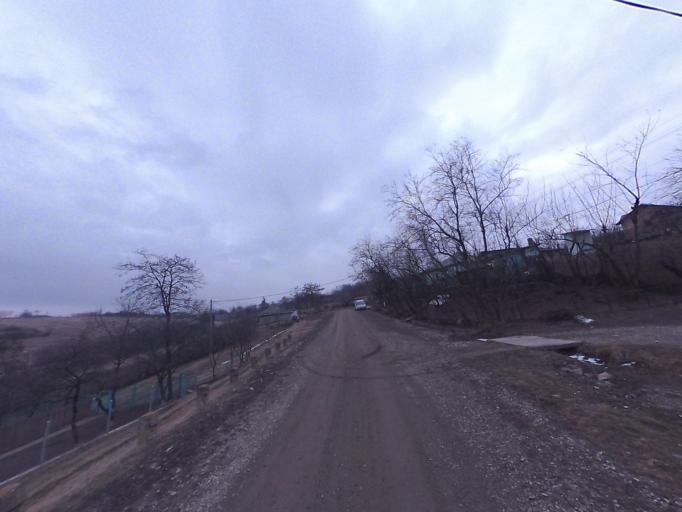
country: RO
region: Iasi
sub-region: Comuna Popricani
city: Popricani
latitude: 47.2956
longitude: 27.5073
